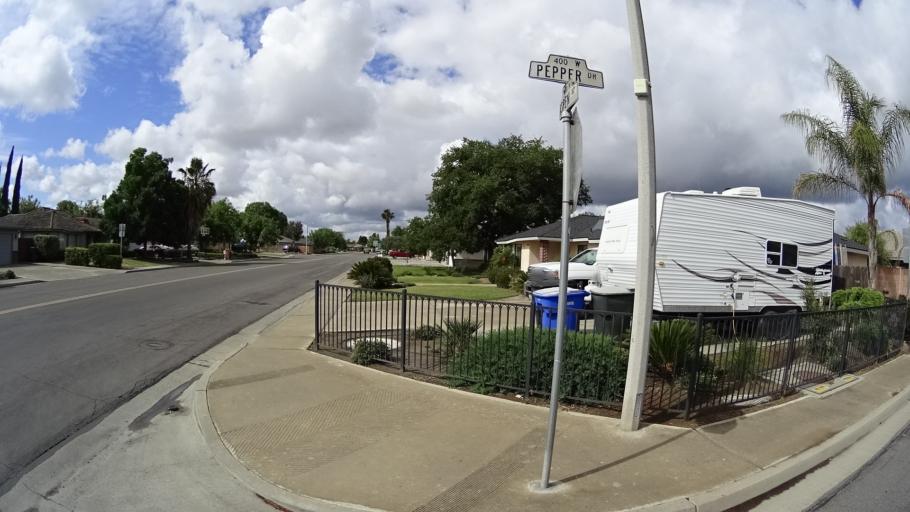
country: US
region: California
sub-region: Kings County
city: Lucerne
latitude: 36.3624
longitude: -119.6501
